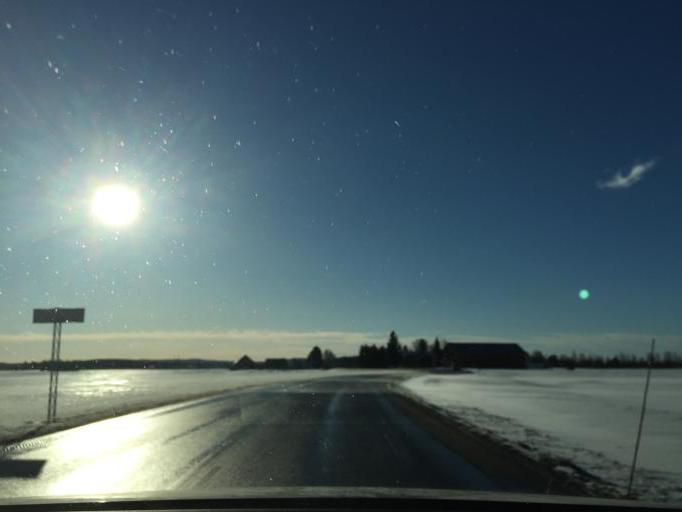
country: NO
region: Akershus
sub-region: Nes
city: Arnes
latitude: 60.1493
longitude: 11.4958
